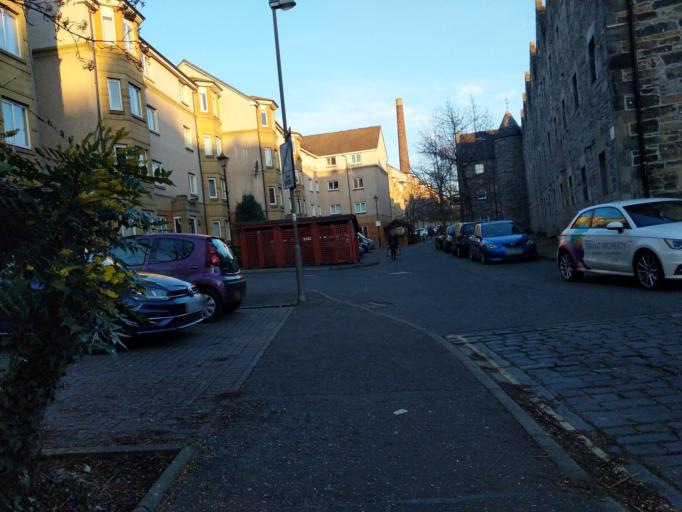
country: GB
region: Scotland
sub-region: Edinburgh
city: Edinburgh
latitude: 55.9433
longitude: -3.2238
